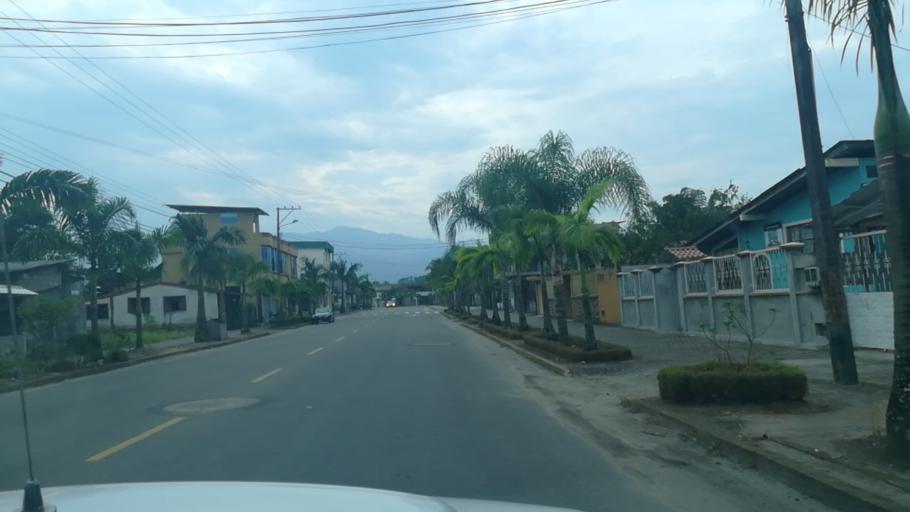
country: EC
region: Napo
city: Tena
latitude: -0.9863
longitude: -77.8158
